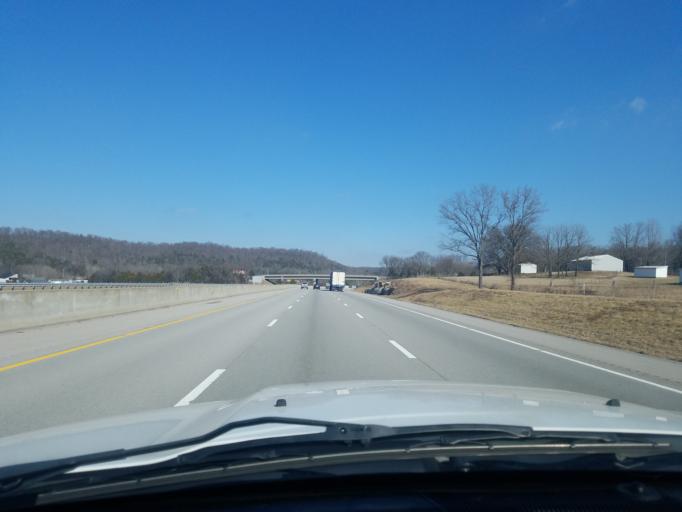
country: US
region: Kentucky
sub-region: Barren County
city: Cave City
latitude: 37.1539
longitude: -85.9708
